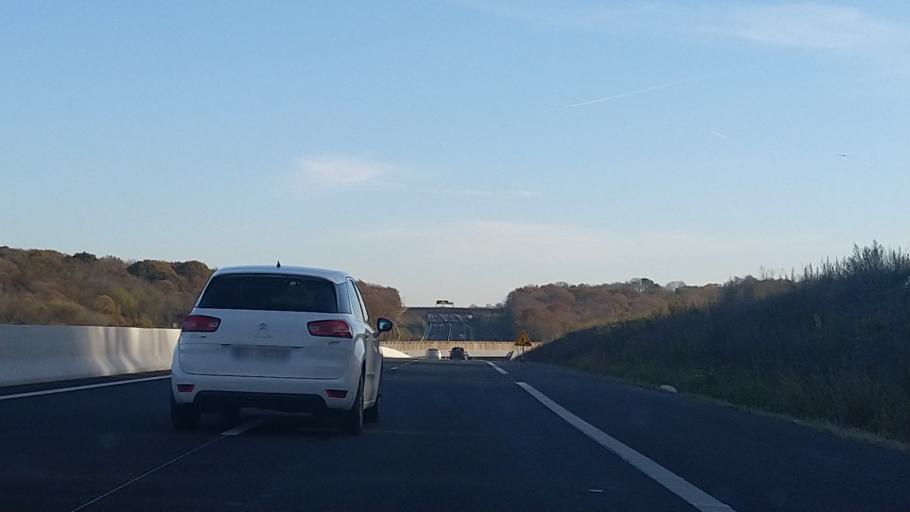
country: FR
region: Ile-de-France
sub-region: Departement du Val-d'Oise
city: Maffliers
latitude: 49.0965
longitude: 2.2962
